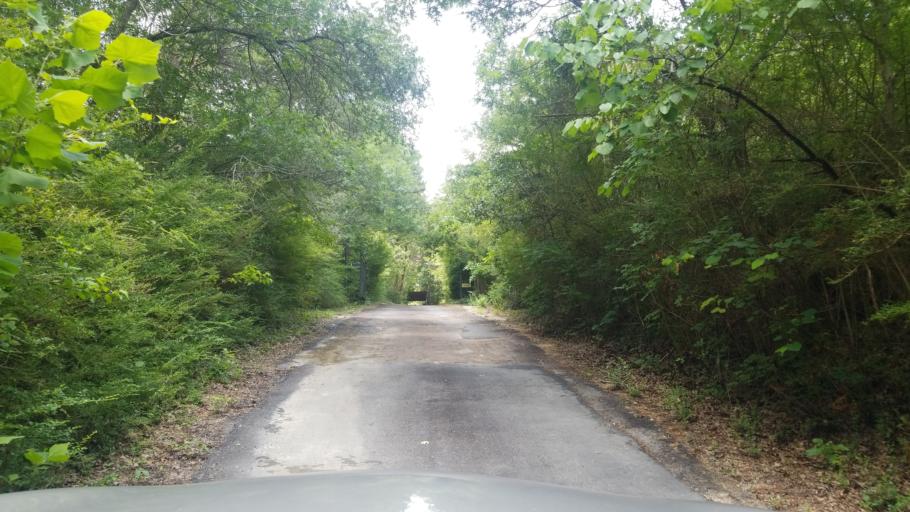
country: US
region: Texas
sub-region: Dallas County
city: Duncanville
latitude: 32.6826
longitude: -96.9185
